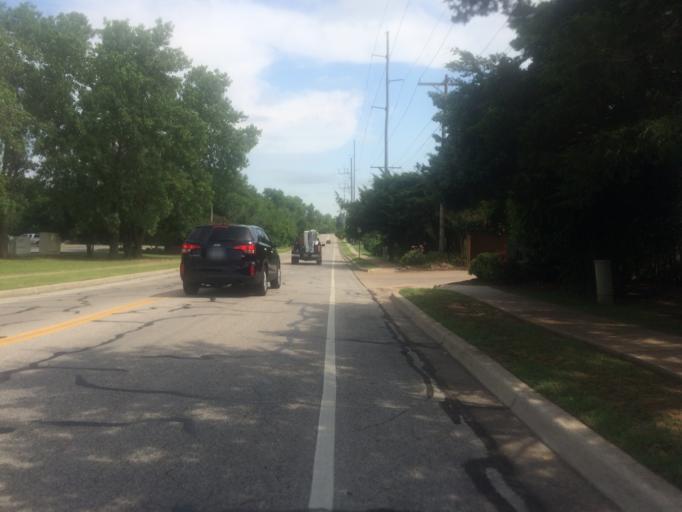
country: US
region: Oklahoma
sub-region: Cleveland County
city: Norman
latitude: 35.1837
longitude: -97.4236
